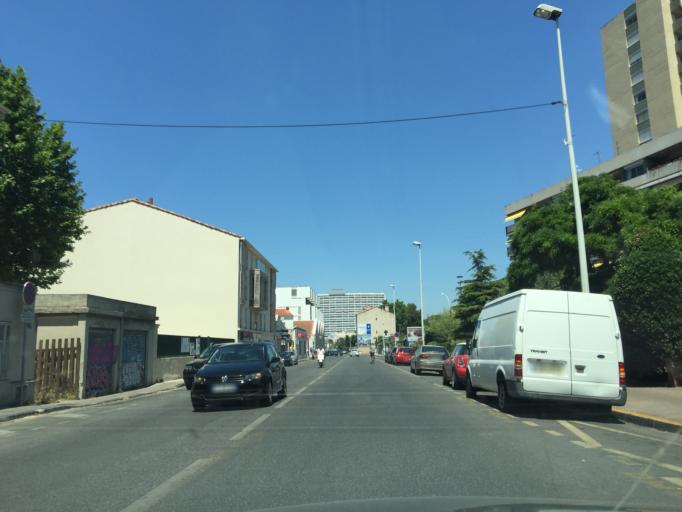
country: FR
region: Provence-Alpes-Cote d'Azur
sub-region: Departement des Bouches-du-Rhone
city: Marseille 09
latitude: 43.2580
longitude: 5.3944
